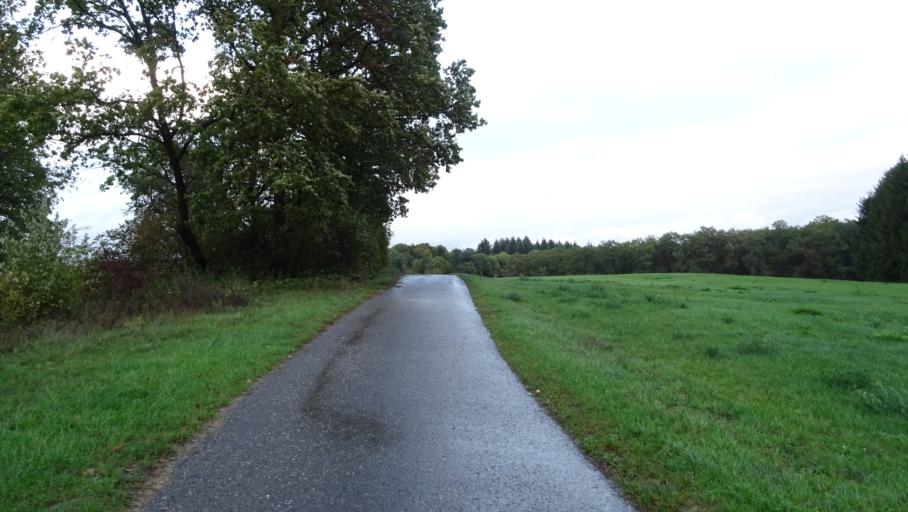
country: DE
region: Baden-Wuerttemberg
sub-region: Karlsruhe Region
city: Binau
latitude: 49.3514
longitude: 9.0478
